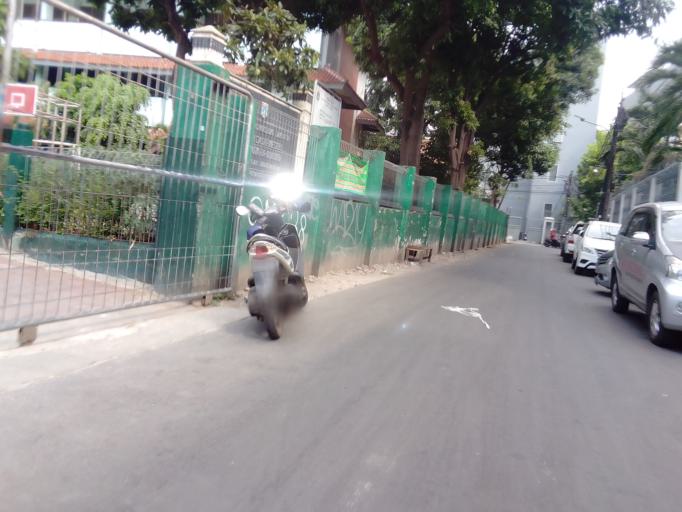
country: ID
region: Jakarta Raya
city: Jakarta
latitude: -6.1643
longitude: 106.8112
